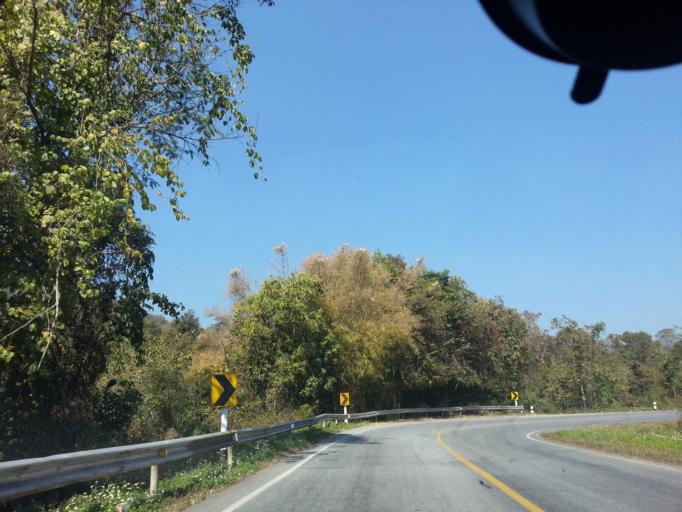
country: TH
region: Chiang Mai
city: Chai Prakan
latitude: 19.5698
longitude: 99.0786
